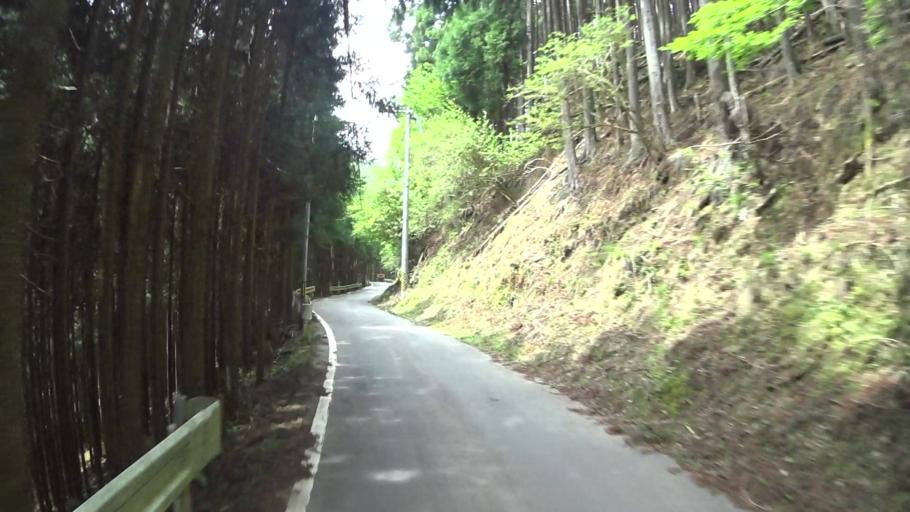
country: JP
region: Kyoto
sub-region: Kyoto-shi
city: Kamigyo-ku
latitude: 35.1785
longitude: 135.7366
